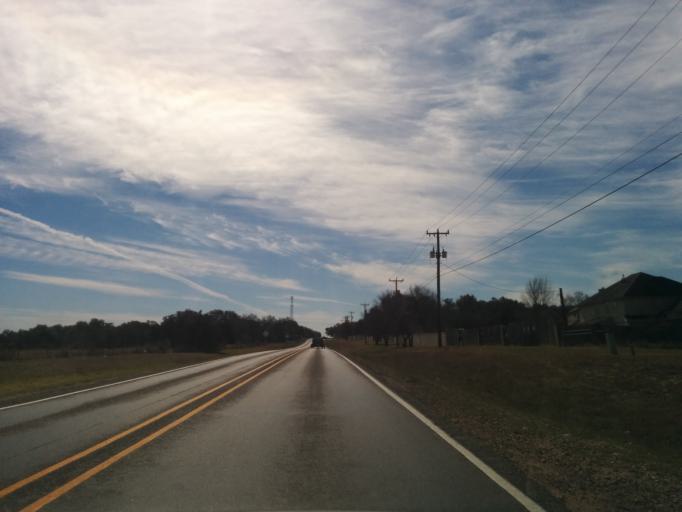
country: US
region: Texas
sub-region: Bexar County
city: Fair Oaks Ranch
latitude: 29.7428
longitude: -98.6233
